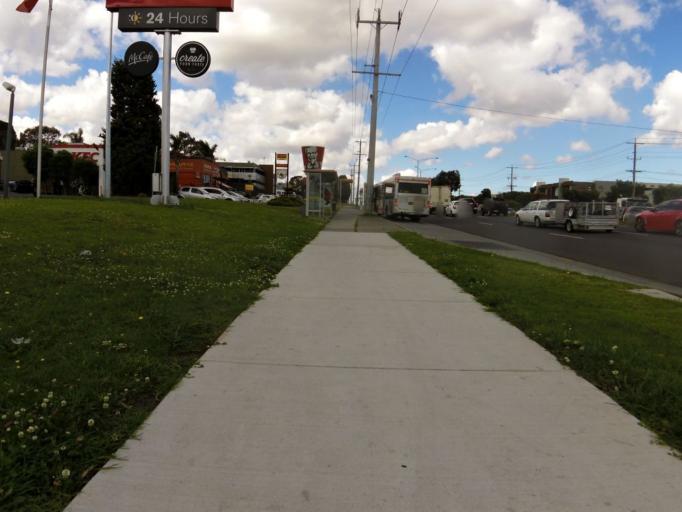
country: AU
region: Victoria
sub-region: Knox
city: Rowville
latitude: -37.9179
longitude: 145.2353
